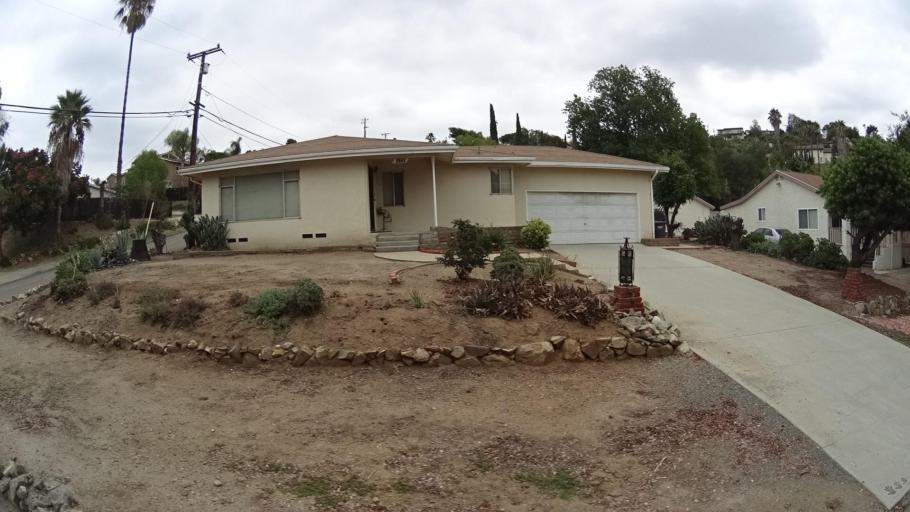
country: US
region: California
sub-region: San Diego County
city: Spring Valley
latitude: 32.7375
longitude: -117.0002
